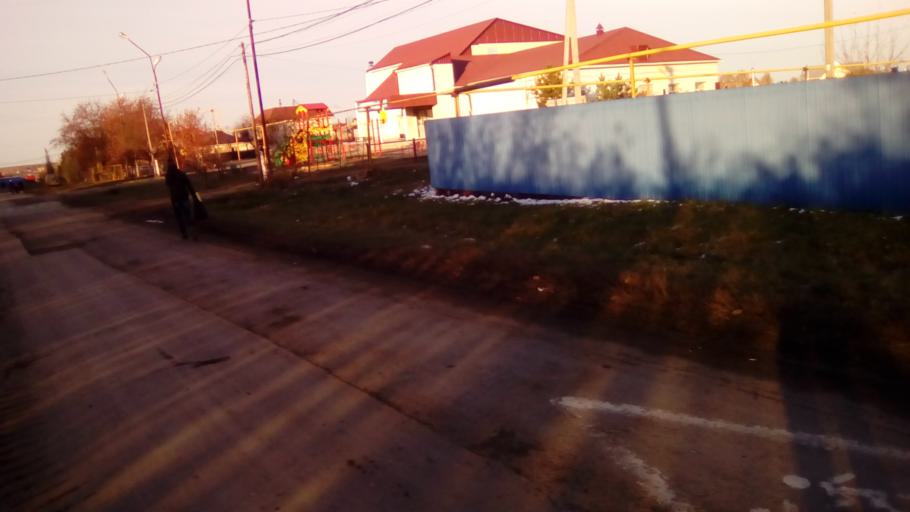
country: RU
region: Tjumen
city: Moskovskiy
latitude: 57.2211
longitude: 65.3591
